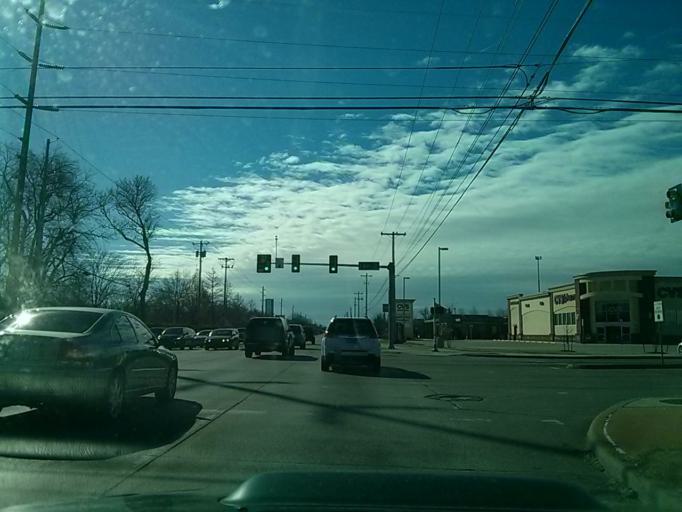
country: US
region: Oklahoma
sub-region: Tulsa County
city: Jenks
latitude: 36.0755
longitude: -95.9582
